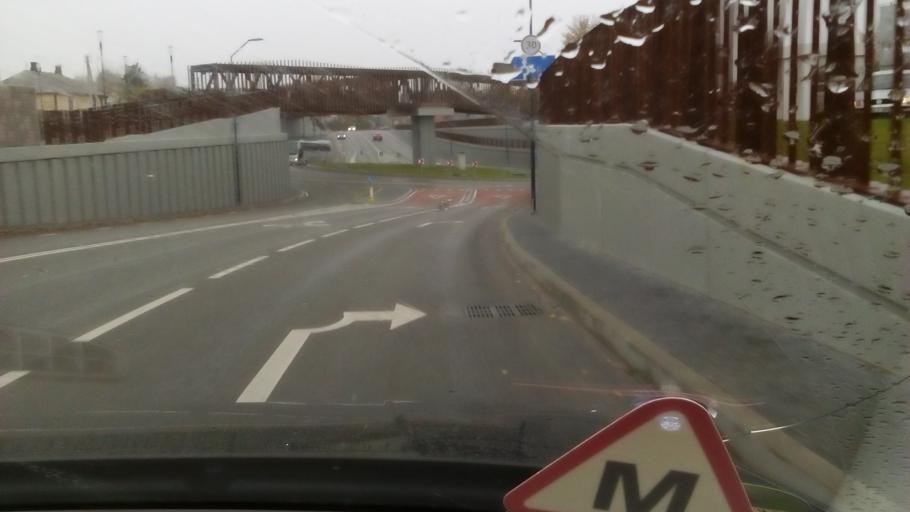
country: LT
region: Marijampoles apskritis
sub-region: Marijampole Municipality
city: Marijampole
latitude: 54.5544
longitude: 23.3619
